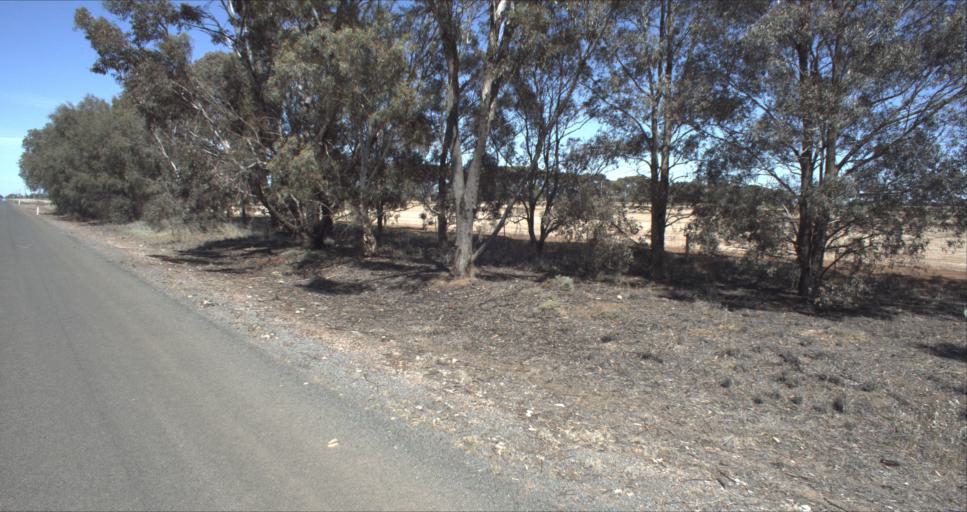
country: AU
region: New South Wales
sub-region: Leeton
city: Leeton
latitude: -34.4719
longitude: 146.2922
